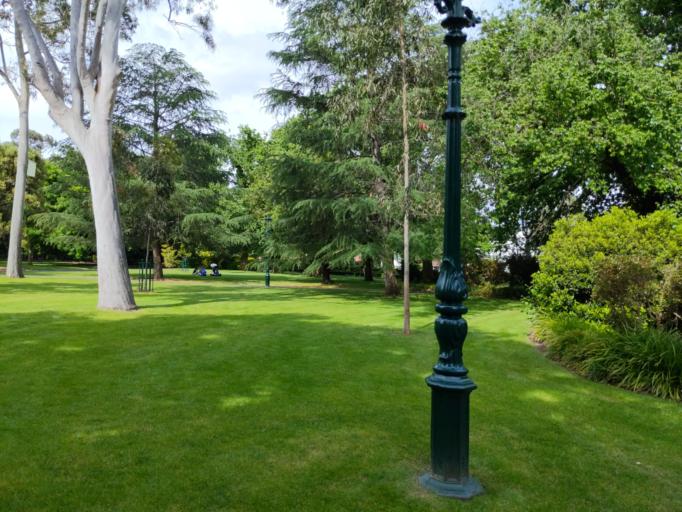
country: AU
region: Victoria
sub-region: Greater Bendigo
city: Bendigo
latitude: -36.7567
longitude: 144.2800
